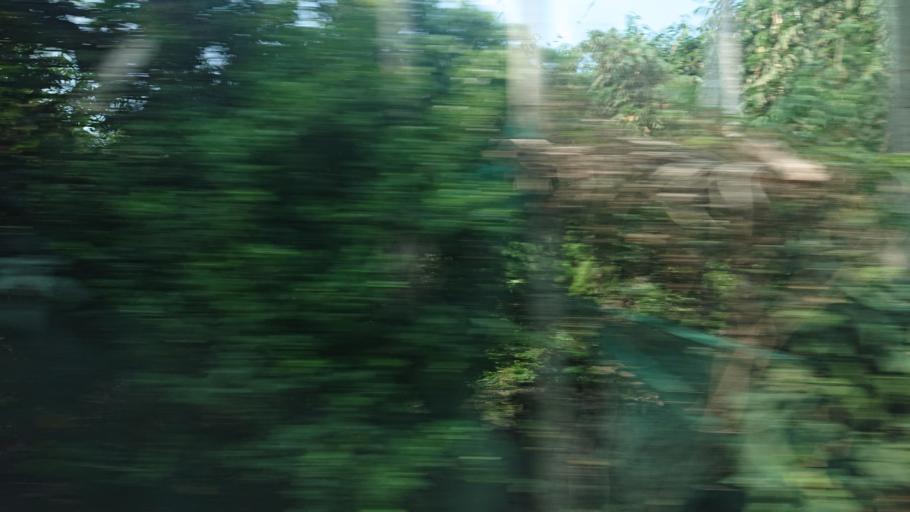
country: TW
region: Taiwan
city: Lugu
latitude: 23.7255
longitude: 120.6675
